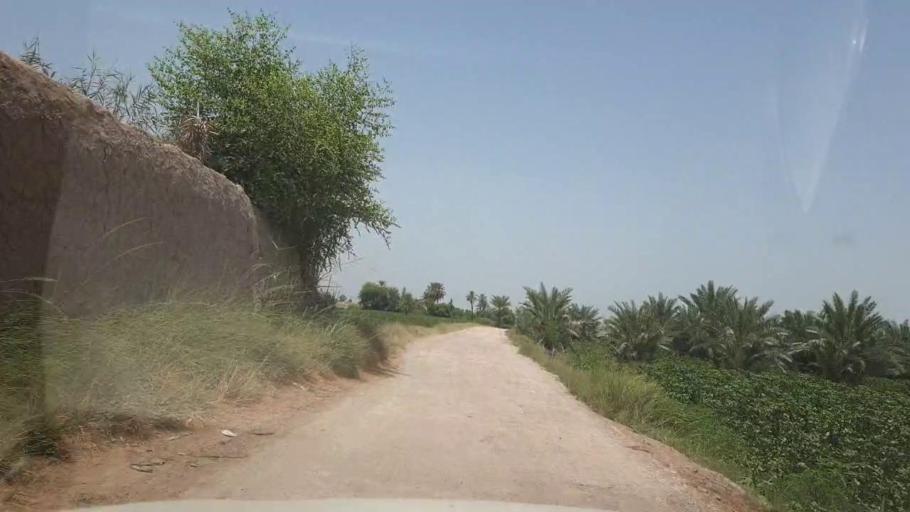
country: PK
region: Sindh
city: Bozdar
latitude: 27.1704
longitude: 68.6259
